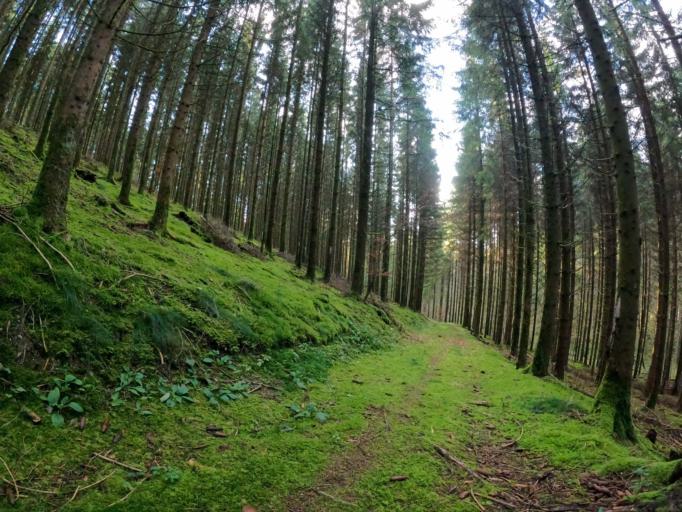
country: LU
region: Diekirch
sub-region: Canton de Wiltz
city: Bavigne
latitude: 49.9726
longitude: 5.8207
